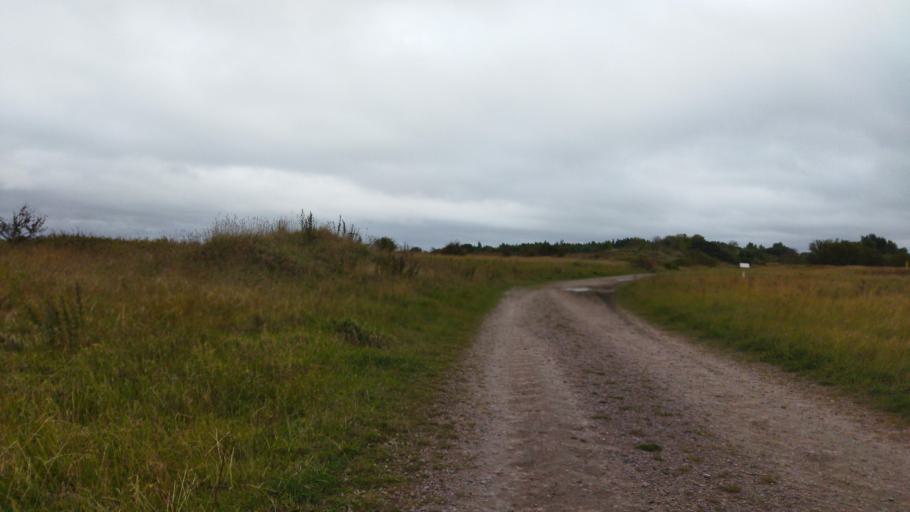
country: NL
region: Groningen
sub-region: Gemeente Delfzijl
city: Delfzijl
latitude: 53.3623
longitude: 7.0012
